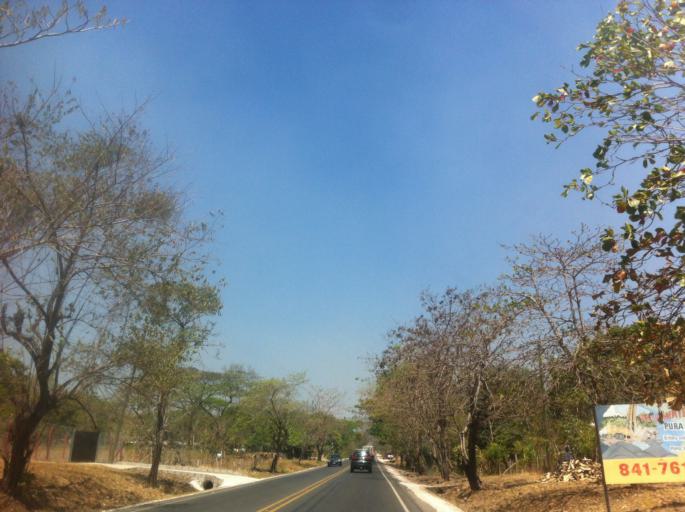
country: CR
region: Guanacaste
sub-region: Canton de Nicoya
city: Nicoya
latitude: 10.1993
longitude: -85.4878
